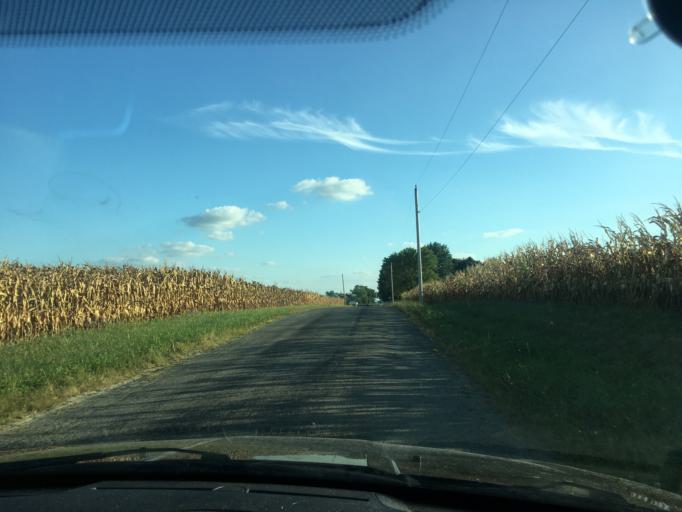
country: US
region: Ohio
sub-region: Logan County
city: West Liberty
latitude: 40.2078
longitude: -83.7403
